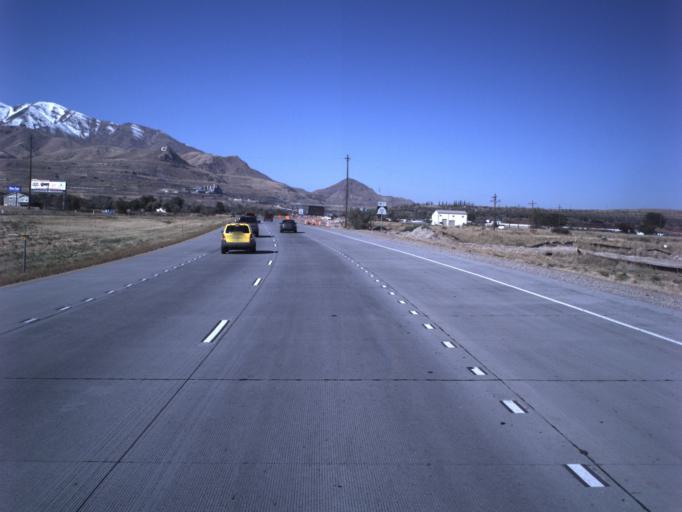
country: US
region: Utah
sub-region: Salt Lake County
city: Magna
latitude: 40.7188
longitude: -112.0643
